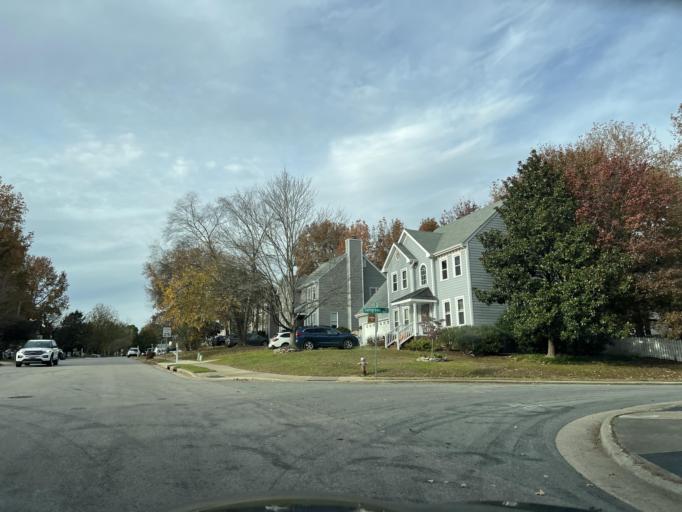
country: US
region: North Carolina
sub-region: Wake County
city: Wake Forest
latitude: 35.9010
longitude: -78.5928
